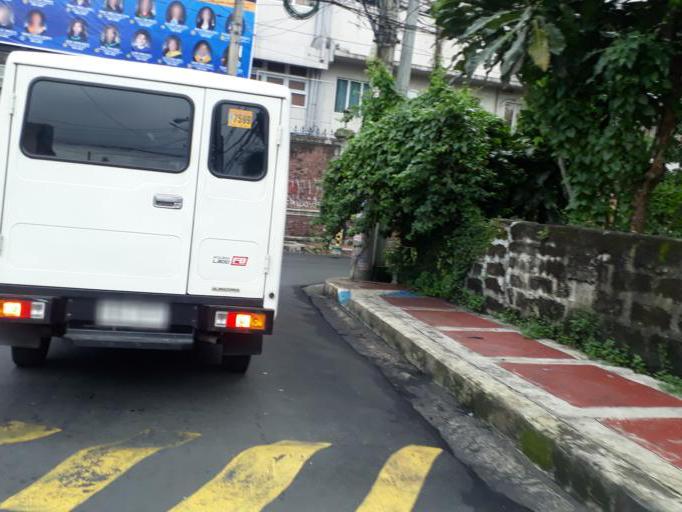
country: PH
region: Metro Manila
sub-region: San Juan
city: San Juan
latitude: 14.6211
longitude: 121.0431
